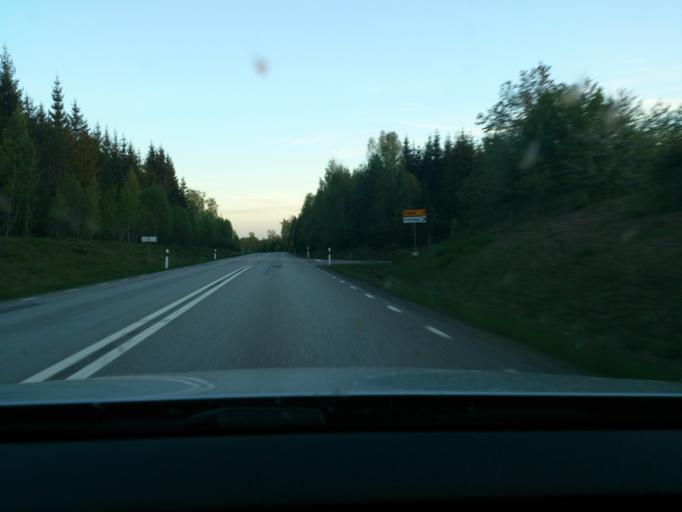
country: SE
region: Kronoberg
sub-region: Alvesta Kommun
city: Moheda
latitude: 57.0769
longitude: 14.6150
